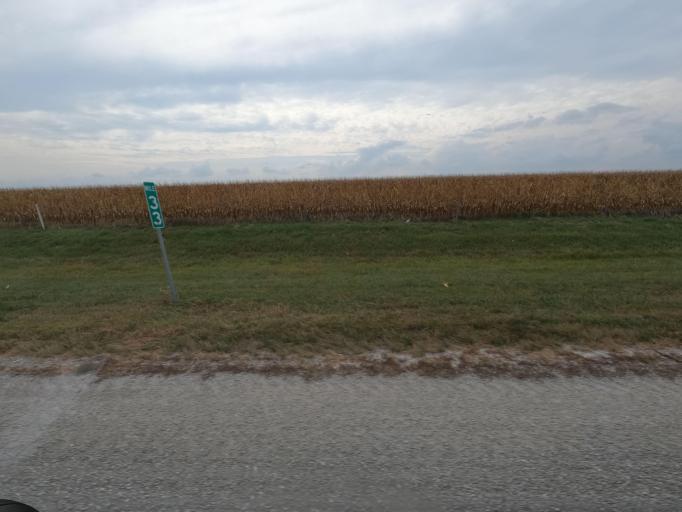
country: US
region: Iowa
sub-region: Jasper County
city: Monroe
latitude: 41.4779
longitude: -93.0510
